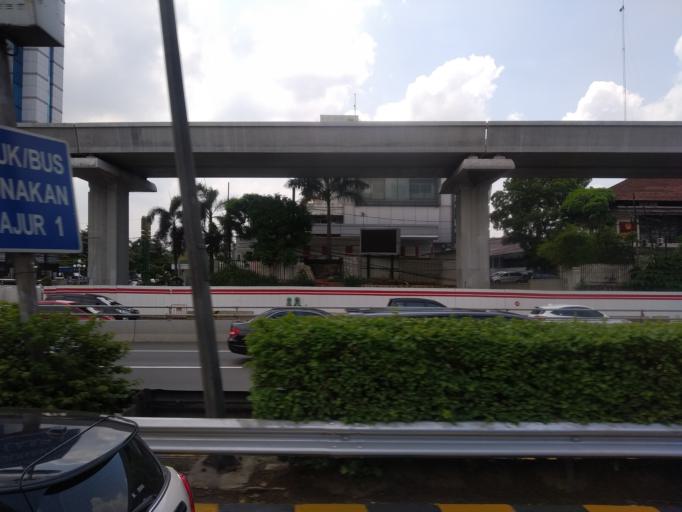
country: ID
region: Jakarta Raya
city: Jakarta
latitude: -6.2434
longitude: 106.8494
